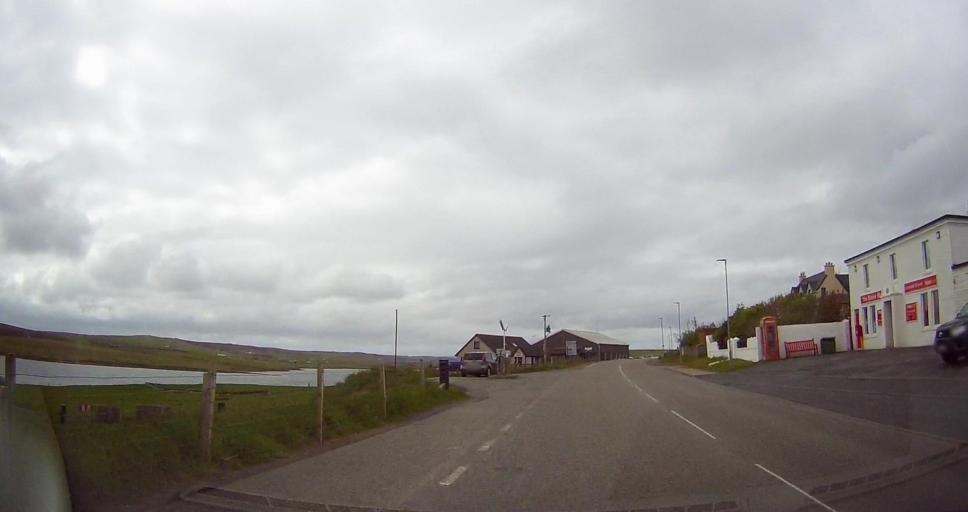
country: GB
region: Scotland
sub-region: Shetland Islands
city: Lerwick
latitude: 60.2529
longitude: -1.4012
